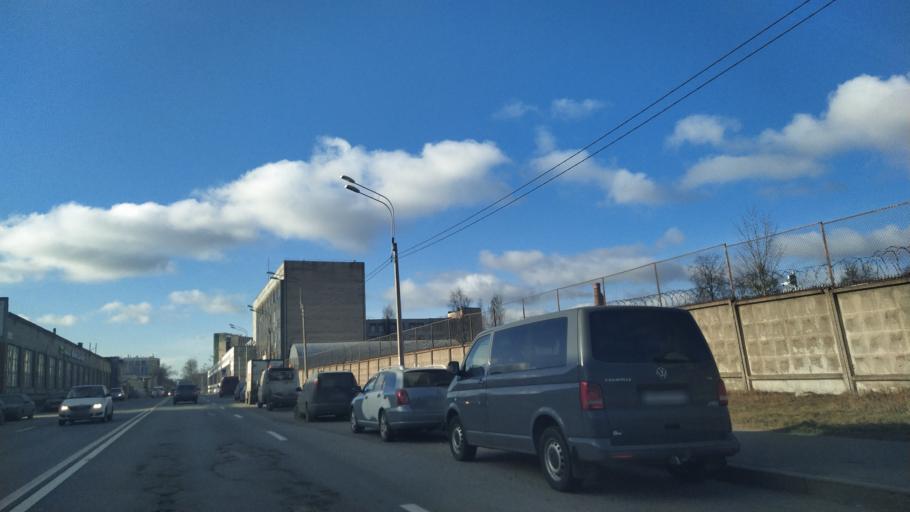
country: RU
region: St.-Petersburg
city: Kushelevka
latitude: 59.9926
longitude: 30.3691
